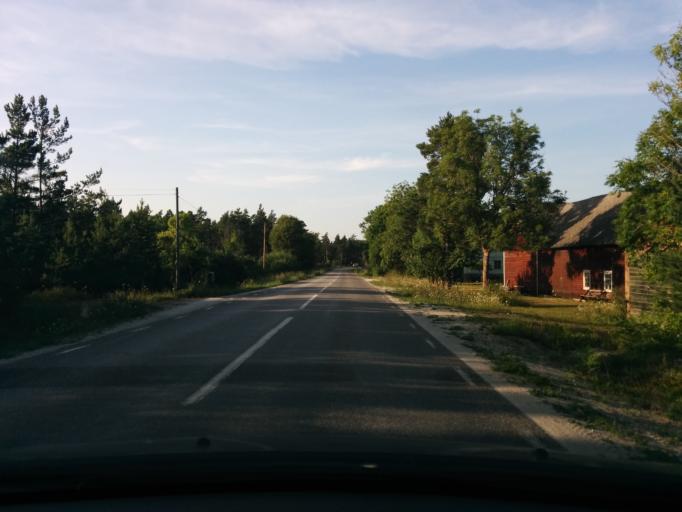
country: SE
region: Gotland
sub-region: Gotland
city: Slite
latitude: 57.5100
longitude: 18.6875
